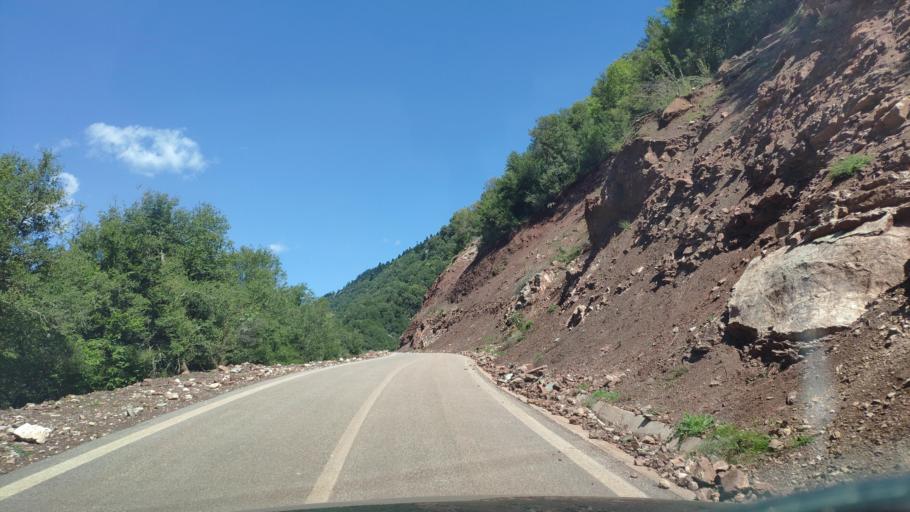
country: GR
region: Central Greece
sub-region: Nomos Evrytanias
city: Kerasochori
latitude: 39.1282
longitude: 21.6268
